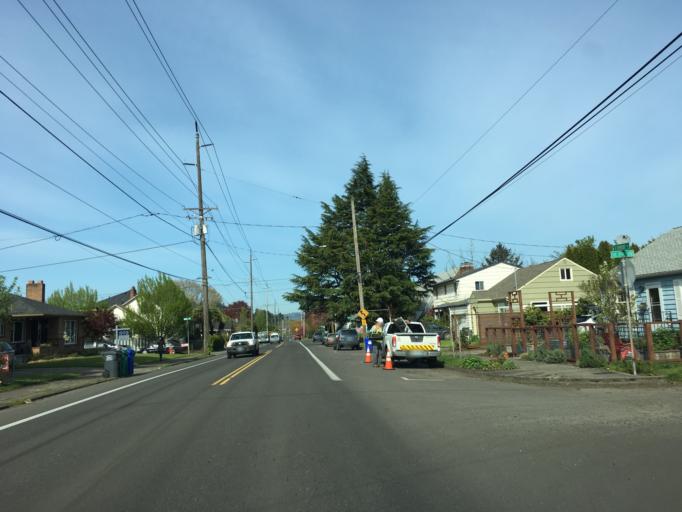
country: US
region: Oregon
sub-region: Multnomah County
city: Lents
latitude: 45.5227
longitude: -122.5721
